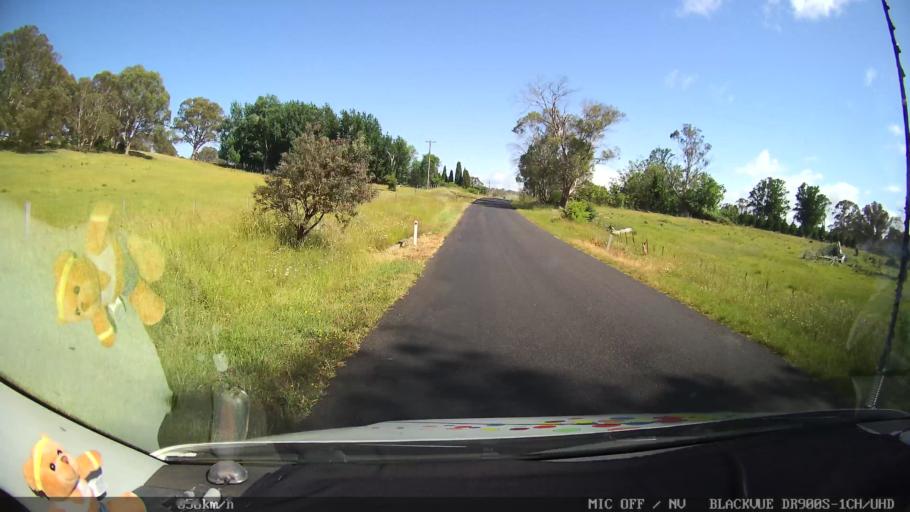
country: AU
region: New South Wales
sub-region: Guyra
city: Guyra
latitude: -30.1039
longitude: 151.6785
